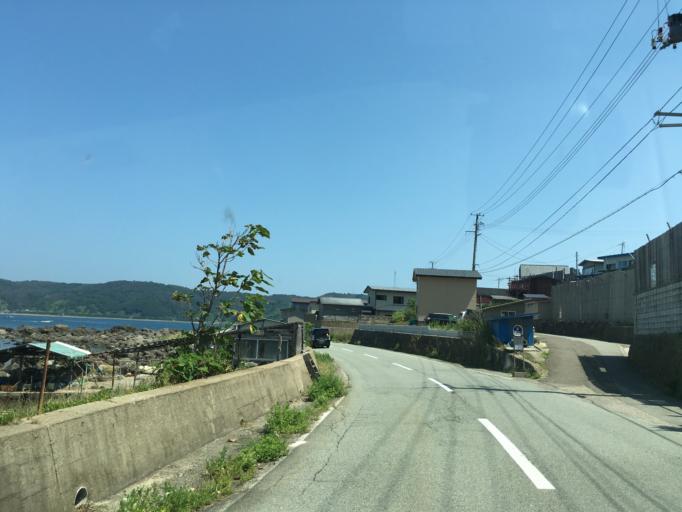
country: JP
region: Akita
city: Tenno
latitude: 39.9448
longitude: 139.7074
